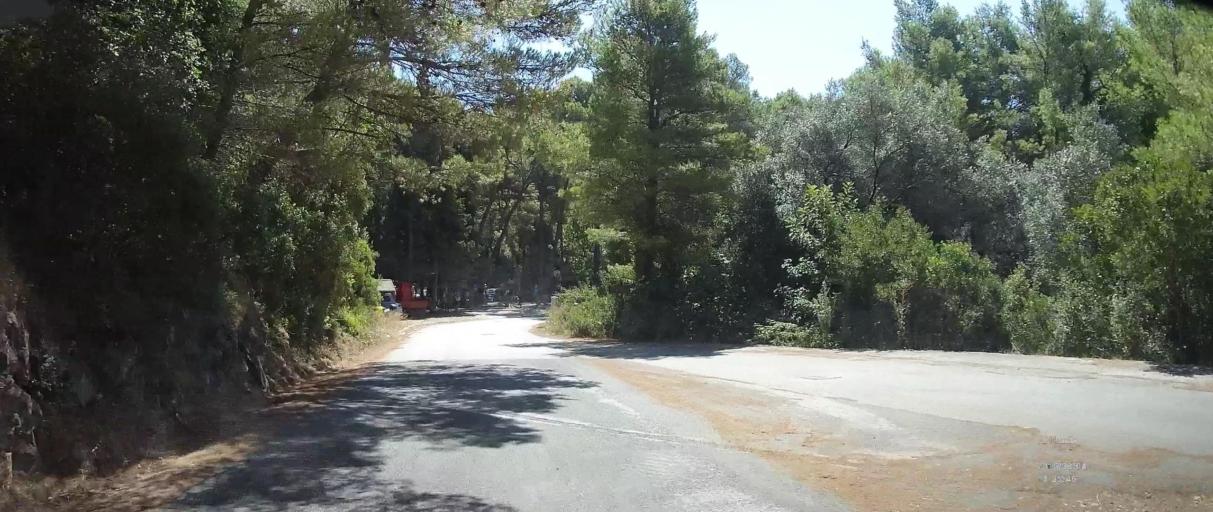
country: HR
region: Dubrovacko-Neretvanska
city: Blato
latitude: 42.7789
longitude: 17.3672
